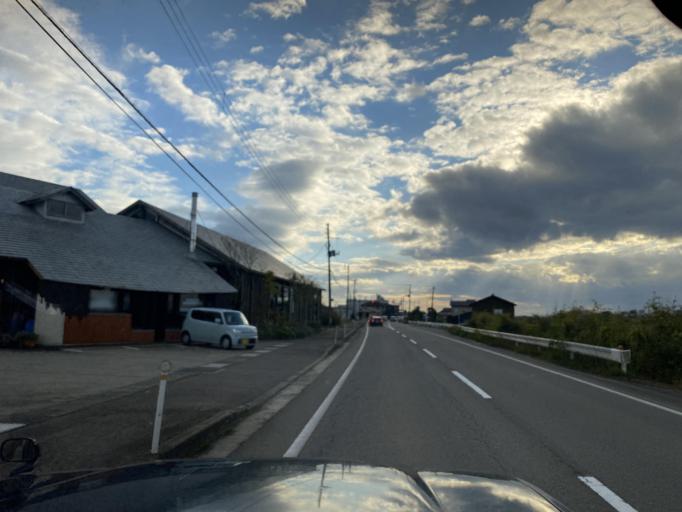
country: JP
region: Niigata
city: Kamo
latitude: 37.6750
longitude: 139.0139
